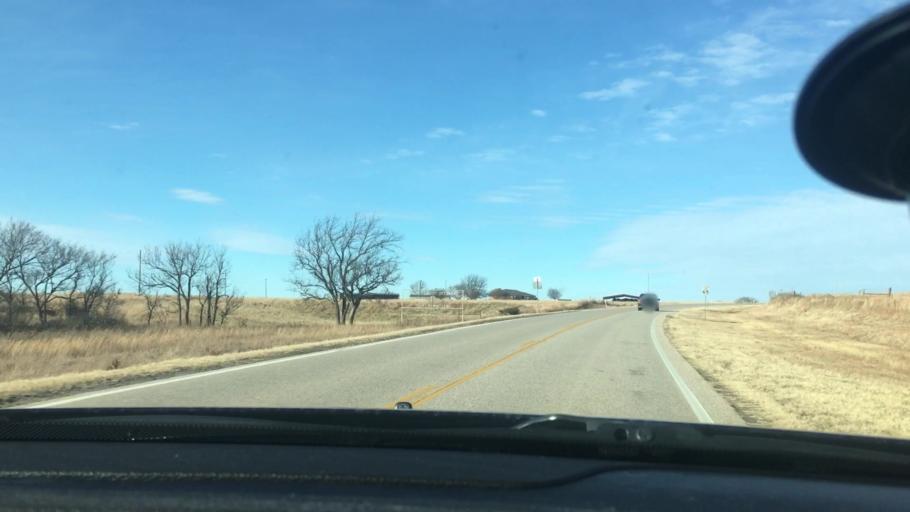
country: US
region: Oklahoma
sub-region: Garvin County
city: Stratford
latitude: 34.9860
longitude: -97.0398
